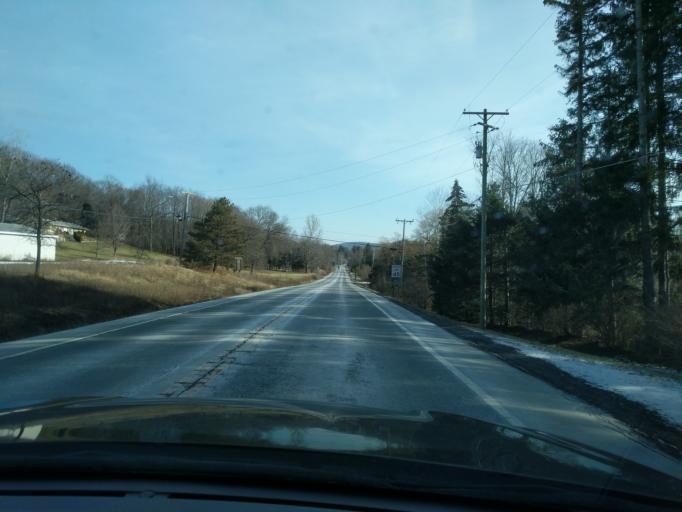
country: US
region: New York
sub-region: Tompkins County
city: East Ithaca
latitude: 42.4021
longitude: -76.4228
